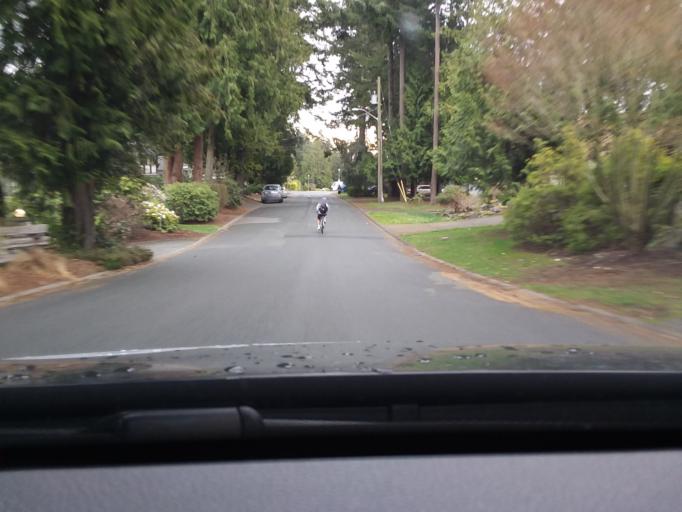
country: CA
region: British Columbia
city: Victoria
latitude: 48.5232
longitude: -123.3812
